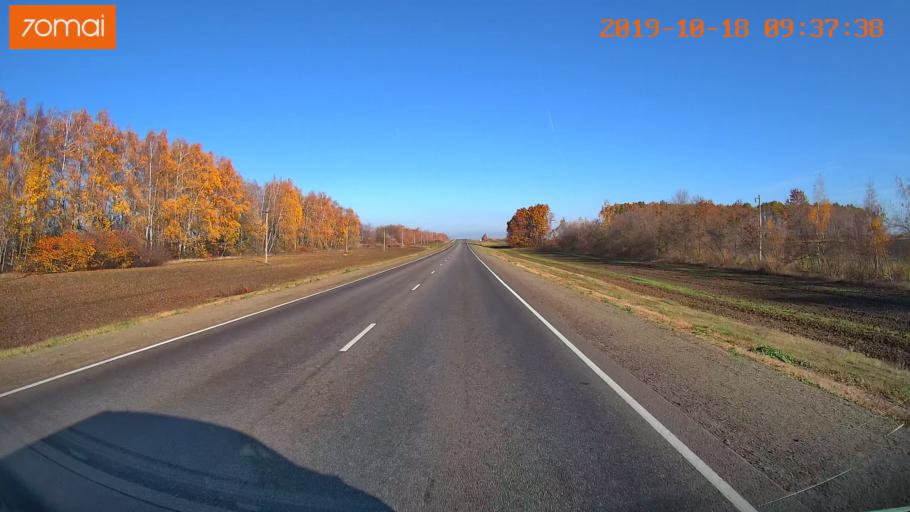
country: RU
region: Tula
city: Yefremov
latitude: 53.2253
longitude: 38.1403
